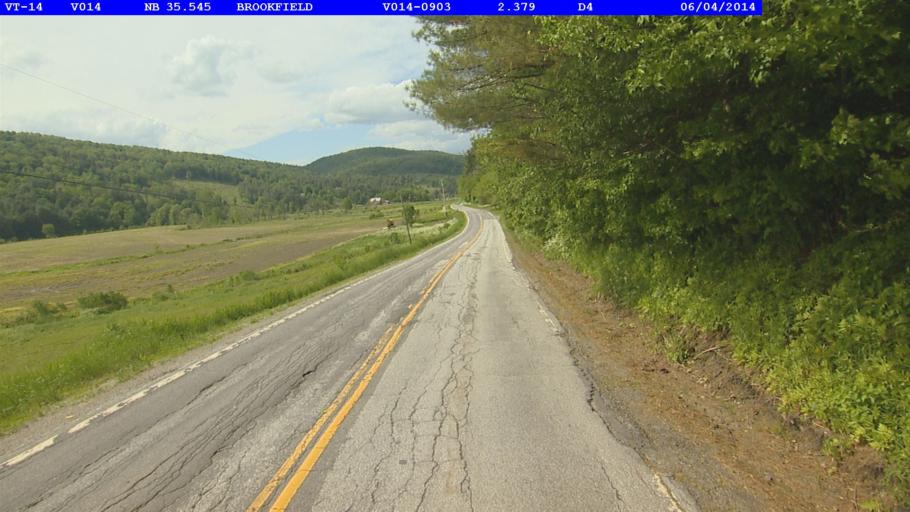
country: US
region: Vermont
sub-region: Orange County
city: Williamstown
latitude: 44.0116
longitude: -72.5675
